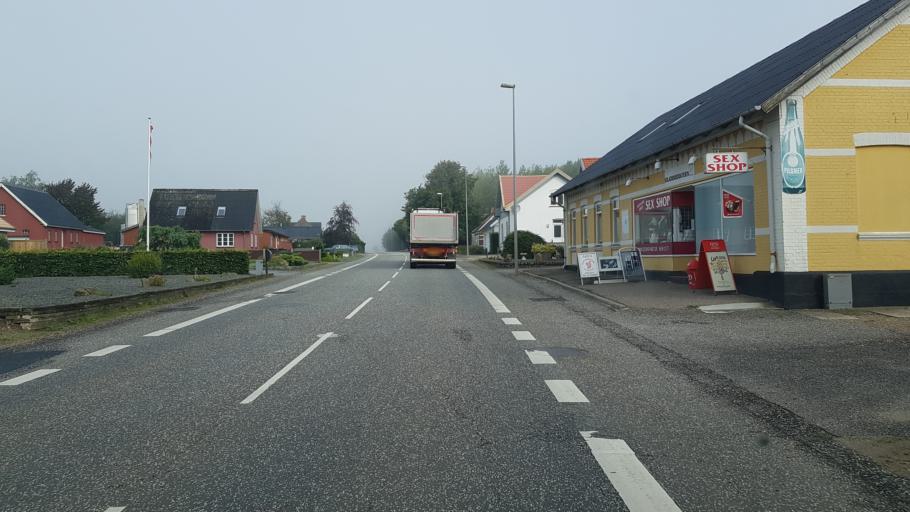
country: DK
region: Central Jutland
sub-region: Viborg Kommune
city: Karup
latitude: 56.3235
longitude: 9.2666
